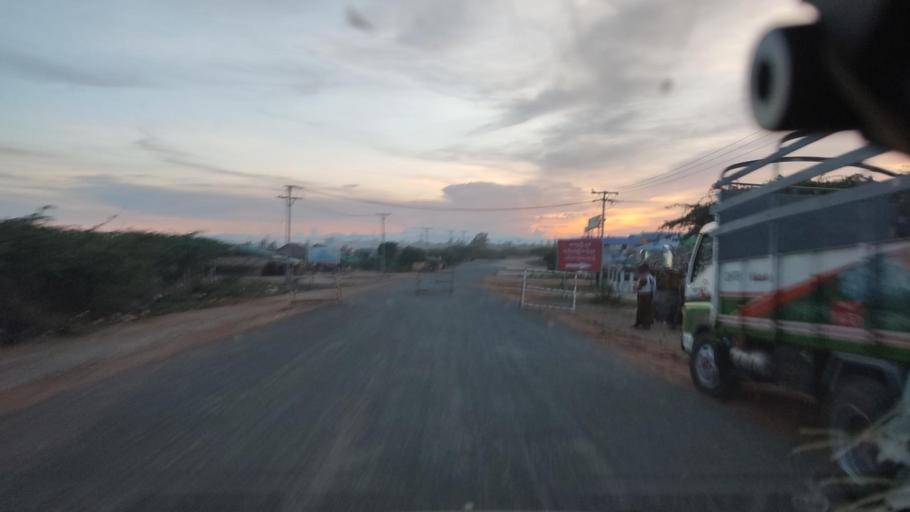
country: MM
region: Magway
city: Magway
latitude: 20.1842
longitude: 94.9433
